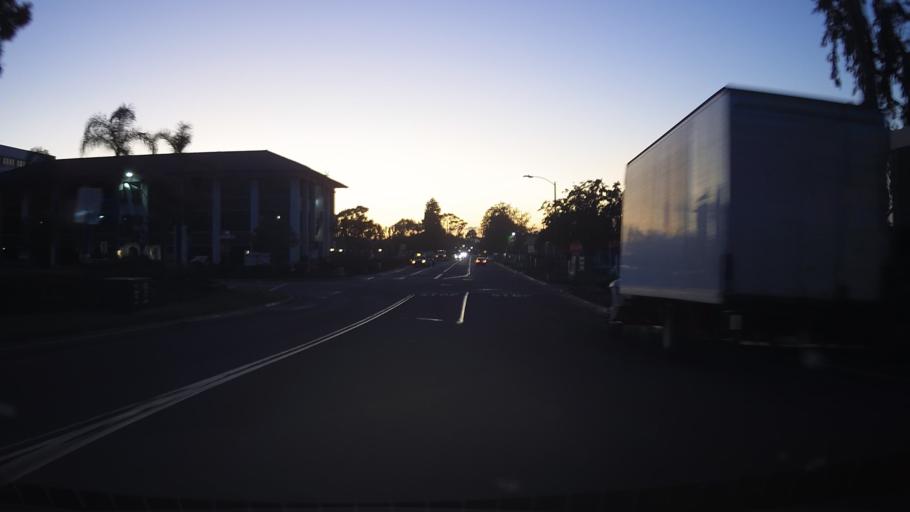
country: US
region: California
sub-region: San Diego County
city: La Jolla
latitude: 32.8347
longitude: -117.1633
